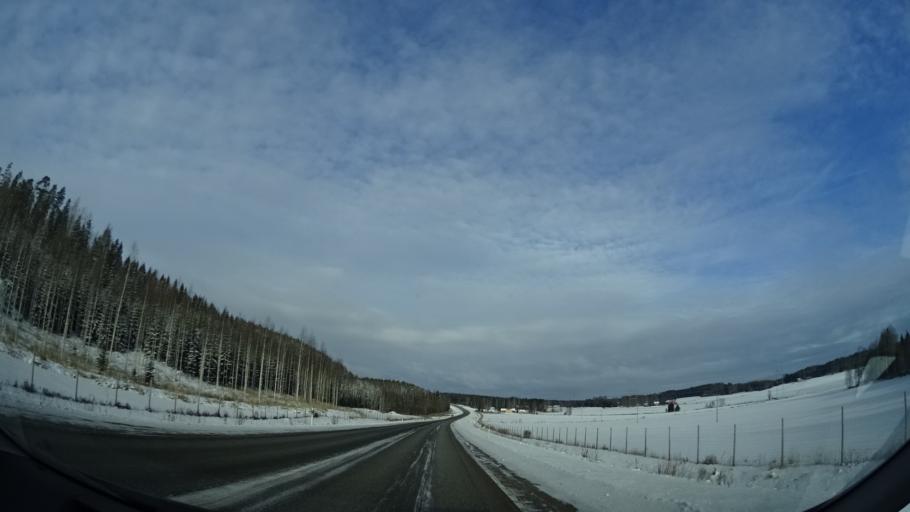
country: FI
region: Uusimaa
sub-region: Helsinki
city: Karkkila
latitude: 60.5800
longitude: 24.1340
